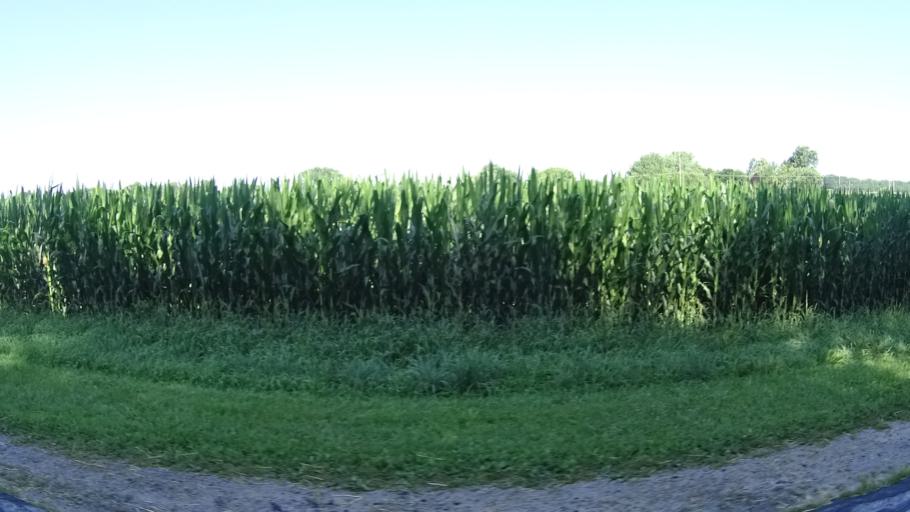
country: US
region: Ohio
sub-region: Huron County
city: Bellevue
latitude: 41.3732
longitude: -82.8193
